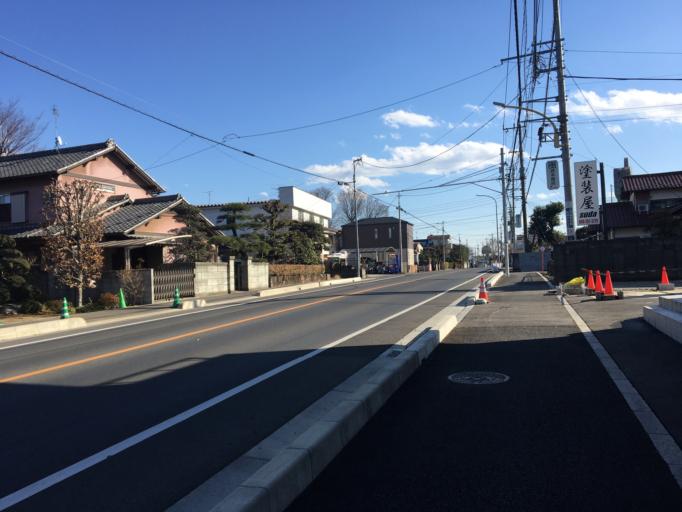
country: JP
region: Saitama
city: Oi
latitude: 35.8474
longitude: 139.5191
